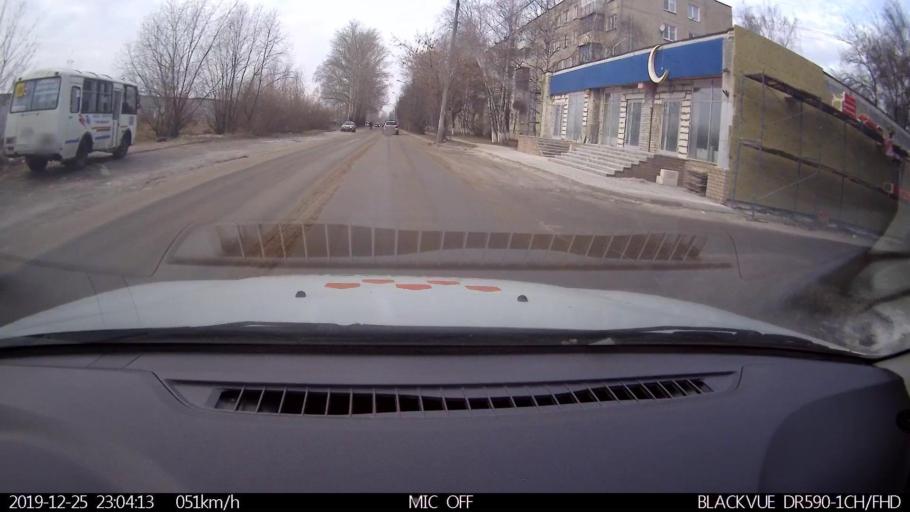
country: RU
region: Nizjnij Novgorod
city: Gorbatovka
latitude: 56.3571
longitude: 43.8127
